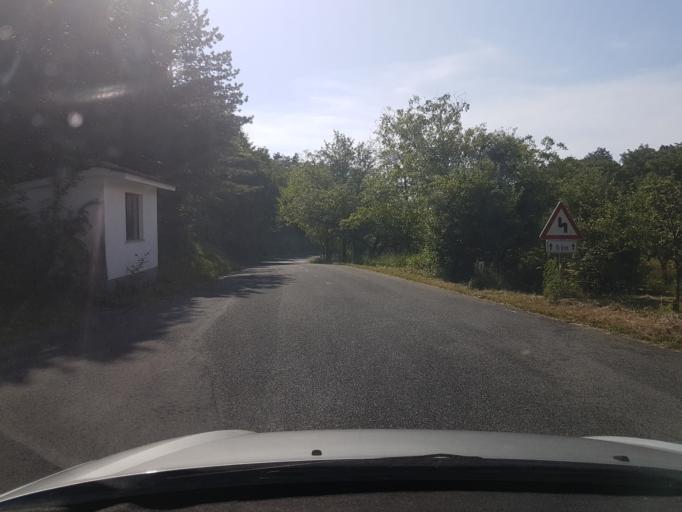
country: SI
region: Vipava
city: Vipava
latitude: 45.7716
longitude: 13.9598
